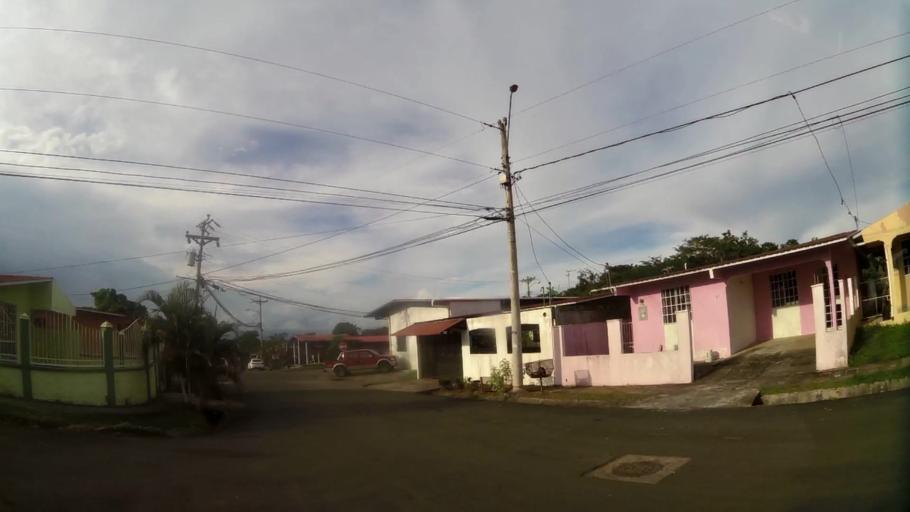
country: PA
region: Panama
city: La Chorrera
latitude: 8.8957
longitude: -79.7672
